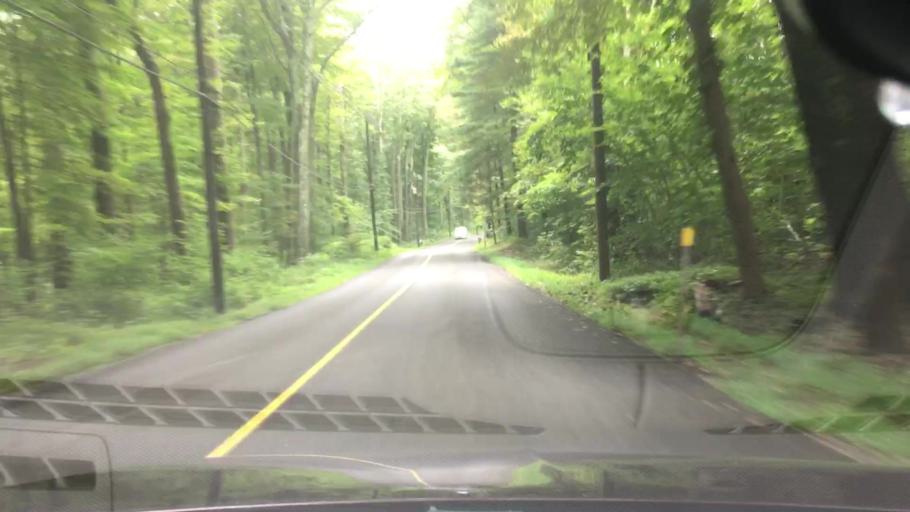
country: US
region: Connecticut
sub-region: New Haven County
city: Madison
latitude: 41.3455
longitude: -72.5644
